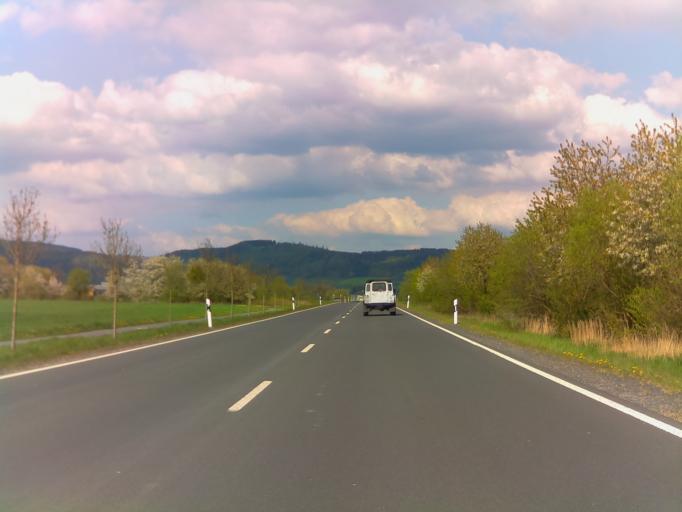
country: DE
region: Thuringia
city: Sonneberg
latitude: 50.3293
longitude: 11.1882
